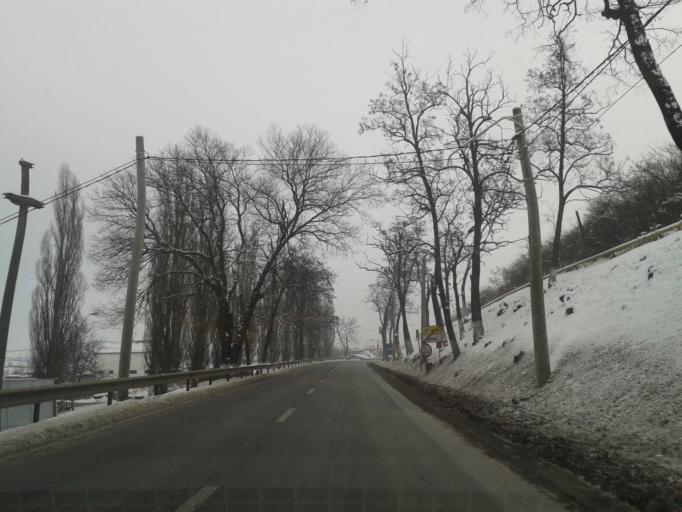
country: RO
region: Hunedoara
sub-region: Municipiul Deva
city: Cristur
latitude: 45.8602
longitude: 22.9320
